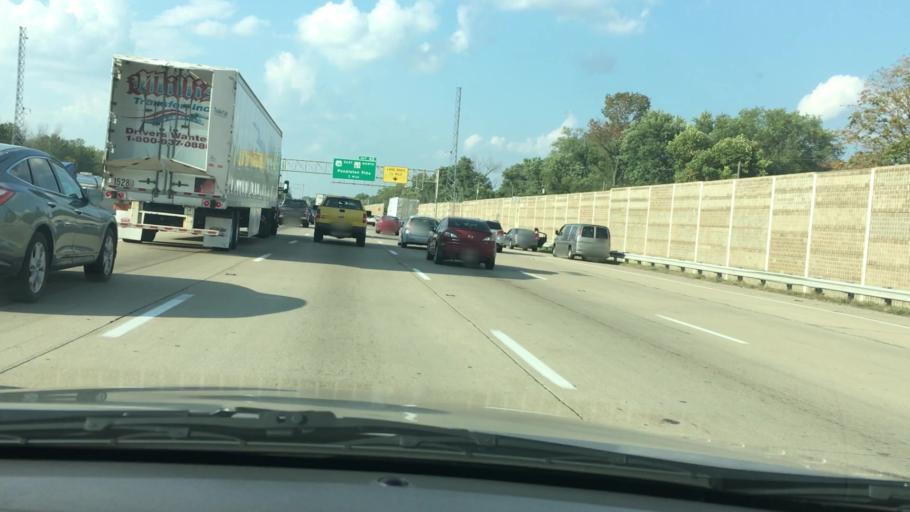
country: US
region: Indiana
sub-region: Marion County
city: Lawrence
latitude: 39.8134
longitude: -86.0307
